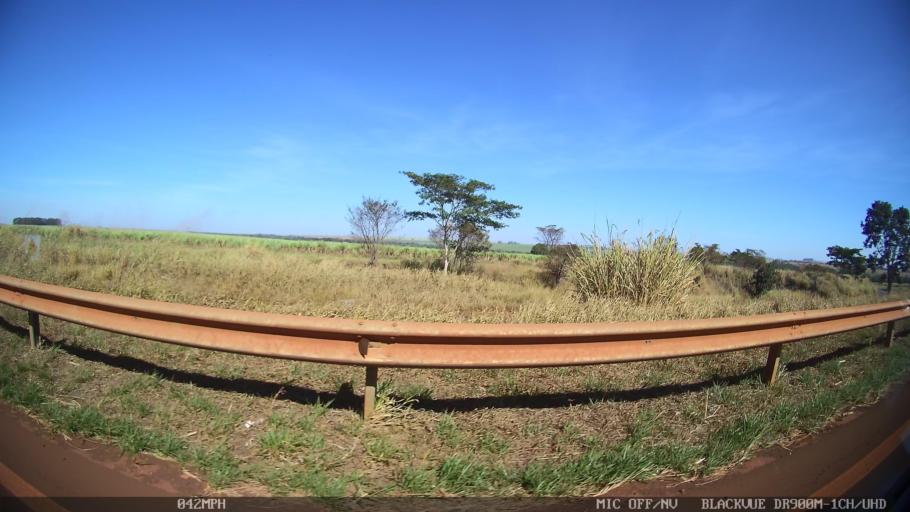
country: BR
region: Sao Paulo
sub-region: Barretos
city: Barretos
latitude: -20.4467
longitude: -48.4484
